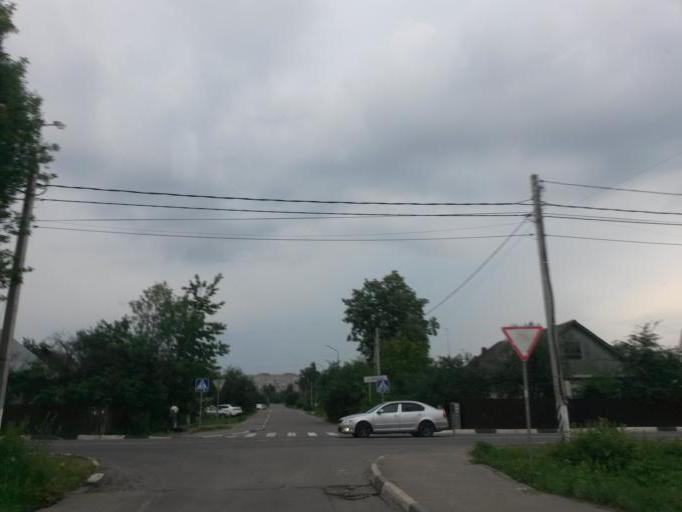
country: RU
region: Moskovskaya
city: Domodedovo
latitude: 55.4318
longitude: 37.7615
